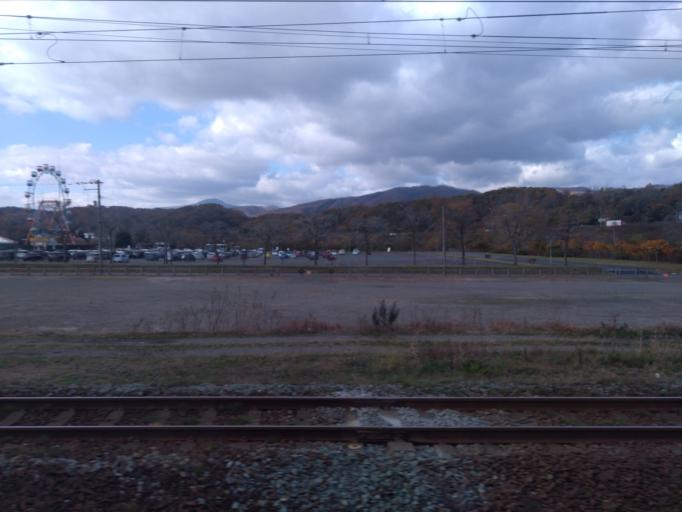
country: JP
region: Hokkaido
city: Shiraoi
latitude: 42.4547
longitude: 141.1855
